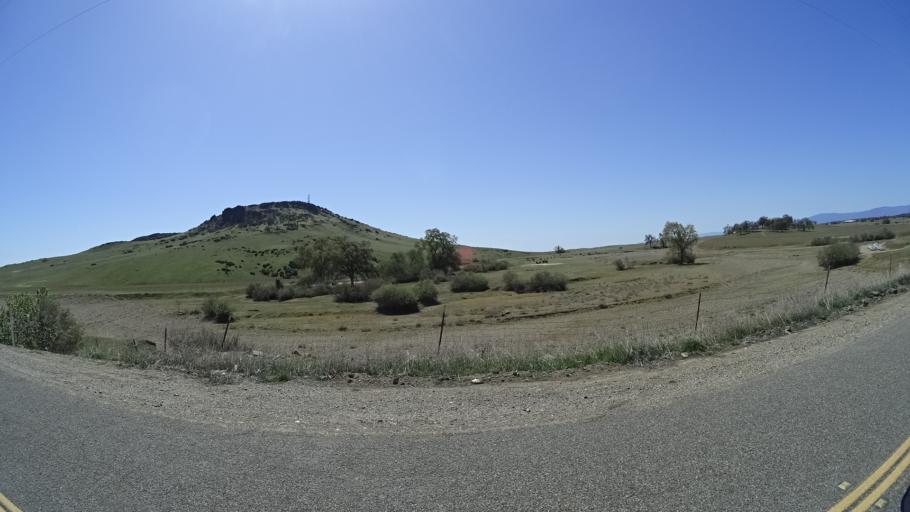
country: US
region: California
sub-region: Glenn County
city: Orland
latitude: 39.7629
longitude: -122.3377
